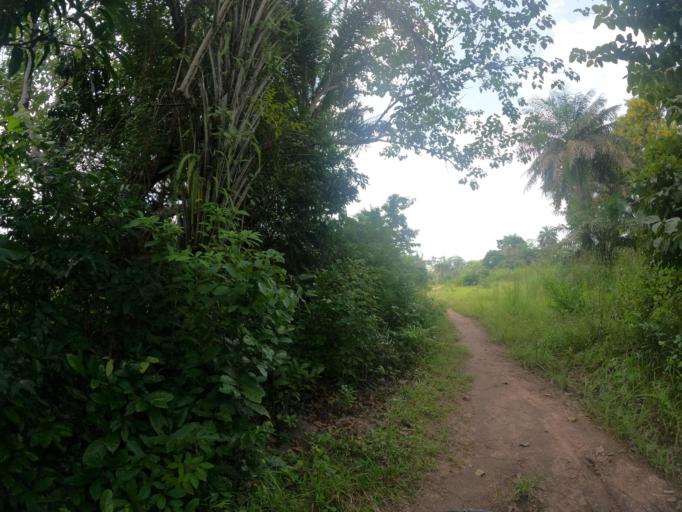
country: SL
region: Northern Province
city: Makeni
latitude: 9.1300
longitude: -12.2711
